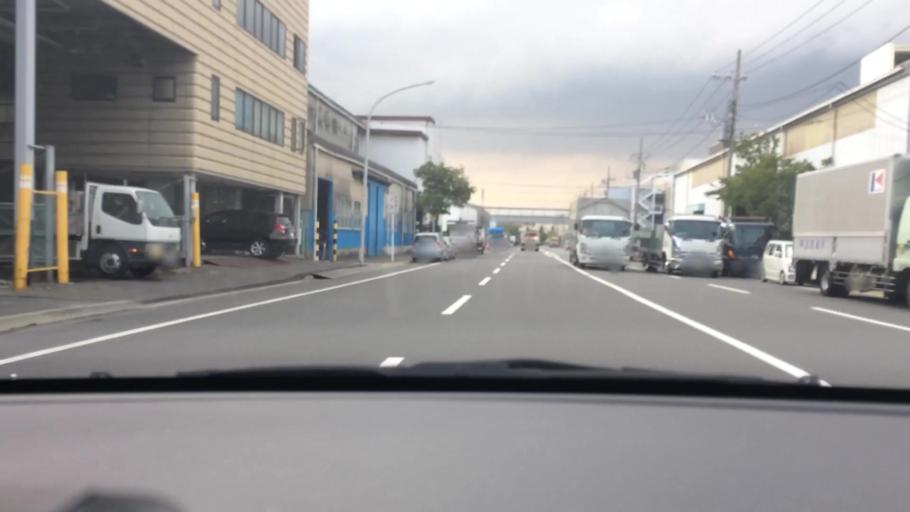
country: JP
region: Tokyo
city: Urayasu
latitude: 35.6354
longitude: 139.9007
